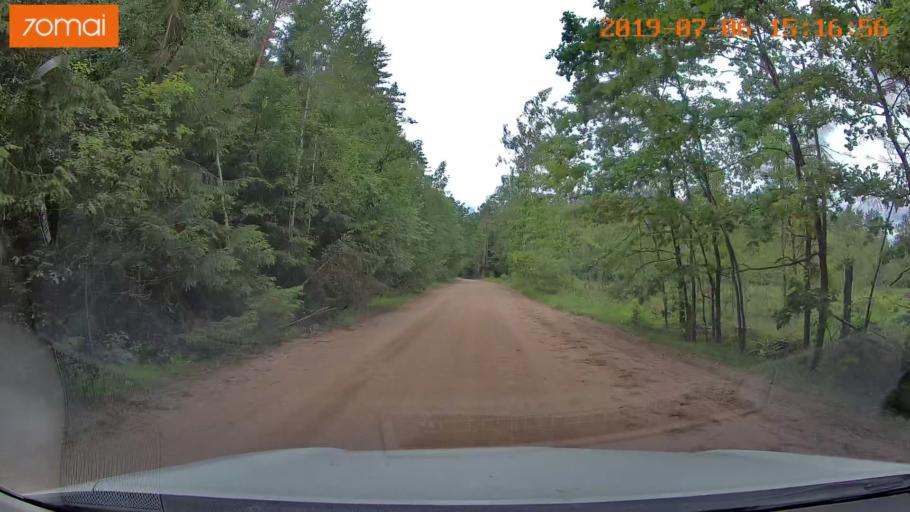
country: BY
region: Minsk
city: Ivyanyets
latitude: 53.9848
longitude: 26.6720
